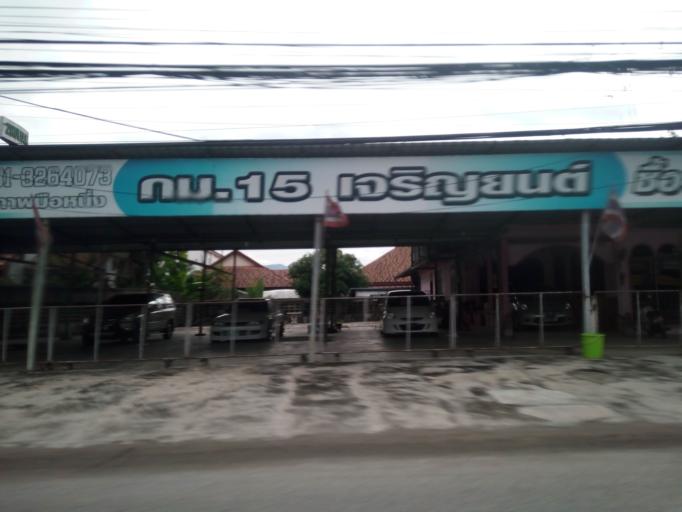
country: TH
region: Phuket
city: Thalang
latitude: 7.9965
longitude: 98.3508
